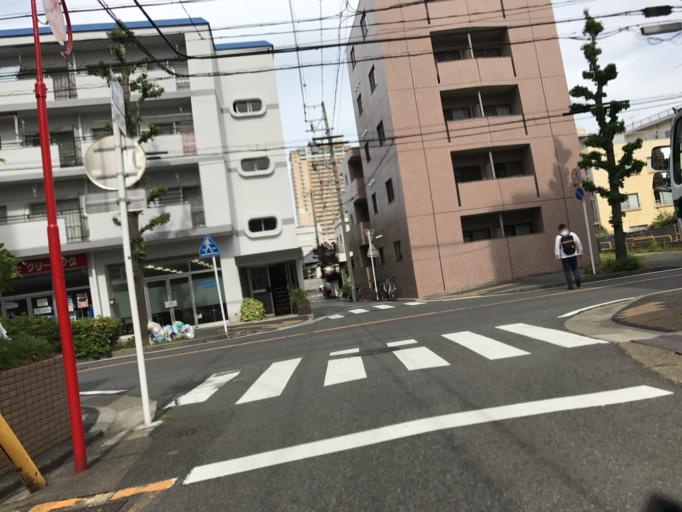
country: JP
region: Aichi
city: Nagoya-shi
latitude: 35.1683
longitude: 136.9331
